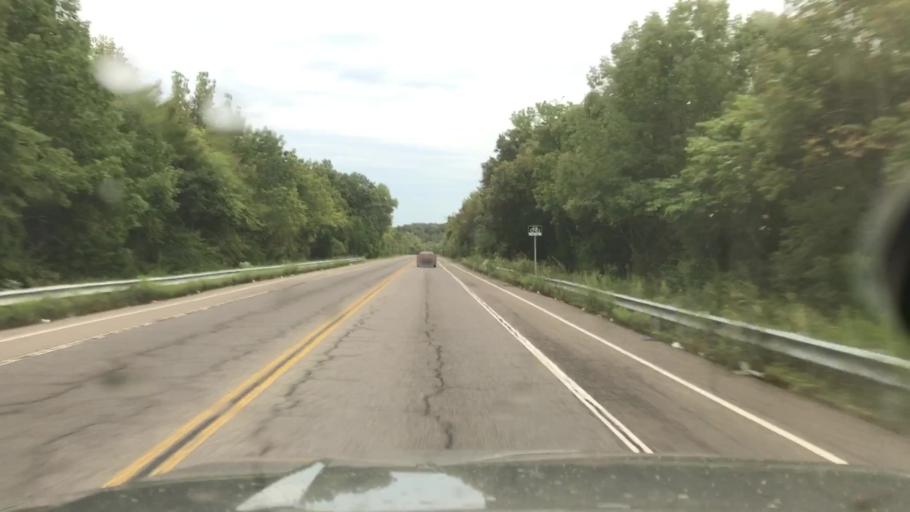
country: US
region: Tennessee
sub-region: Rutherford County
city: La Vergne
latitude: 36.1047
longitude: -86.6284
